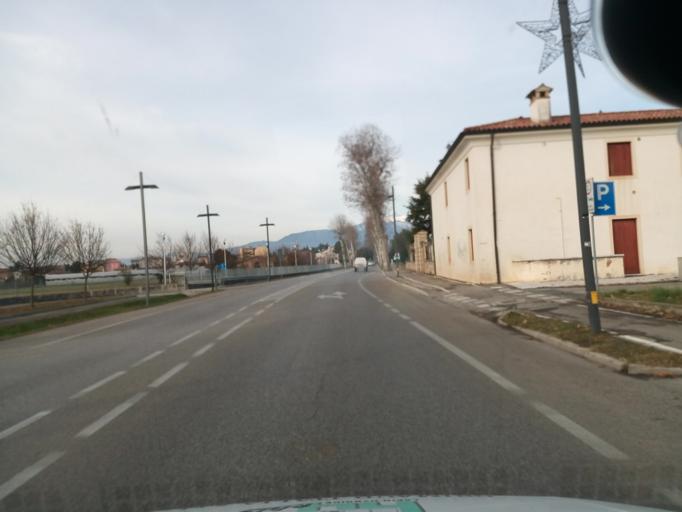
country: IT
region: Veneto
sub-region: Provincia di Treviso
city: Caerano di San Marco
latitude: 45.7837
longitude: 12.0112
